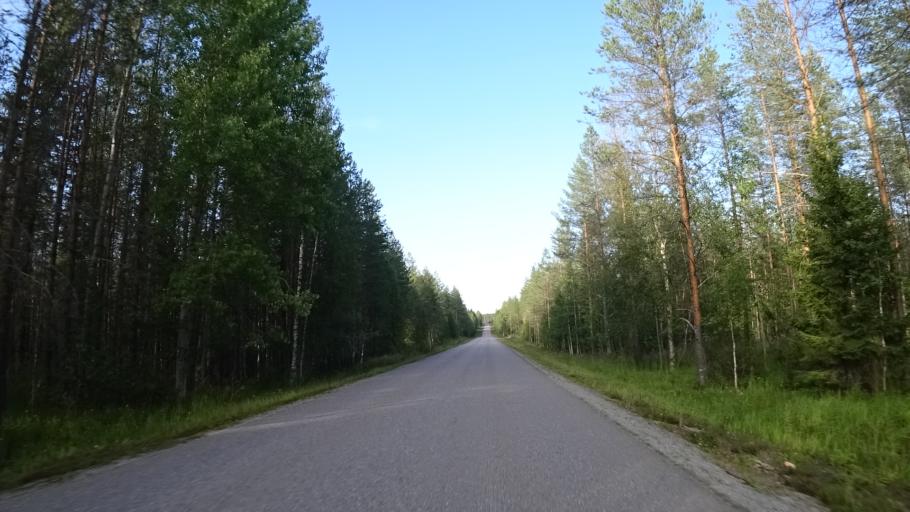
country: FI
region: North Karelia
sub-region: Joensuu
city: Eno
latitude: 63.0610
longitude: 30.5460
